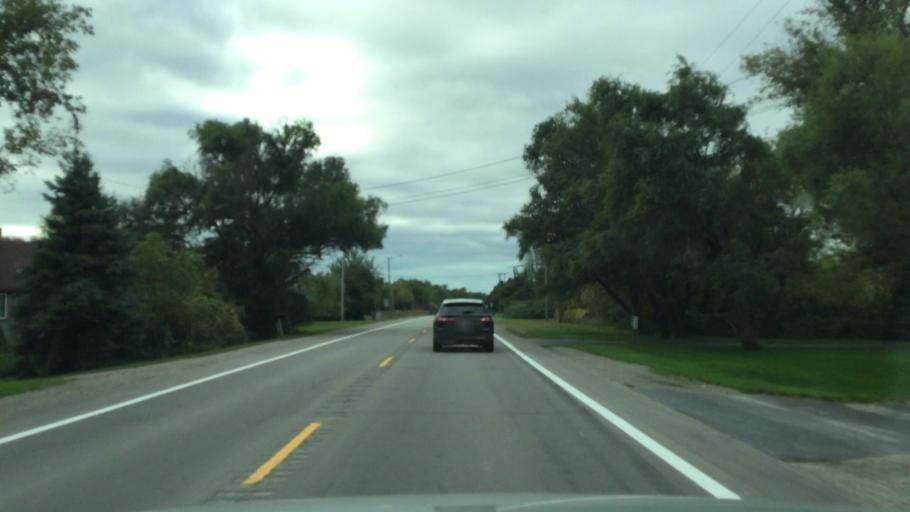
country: US
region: Michigan
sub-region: Macomb County
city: Richmond
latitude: 42.8402
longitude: -82.7618
